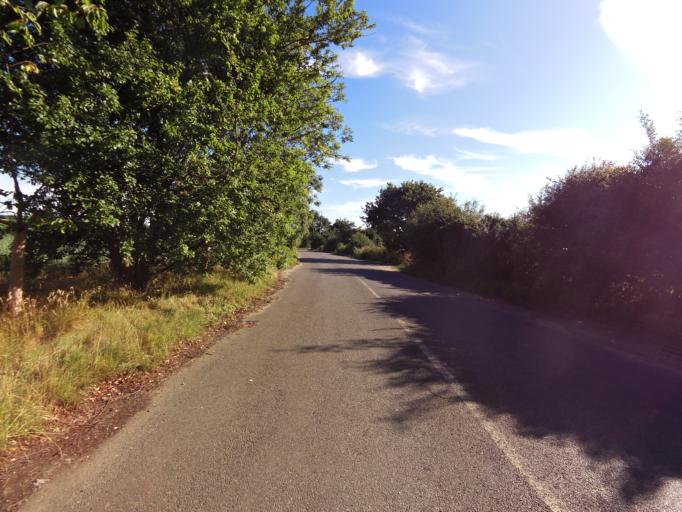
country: GB
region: England
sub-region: Suffolk
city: Kesgrave
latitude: 52.0492
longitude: 1.2780
